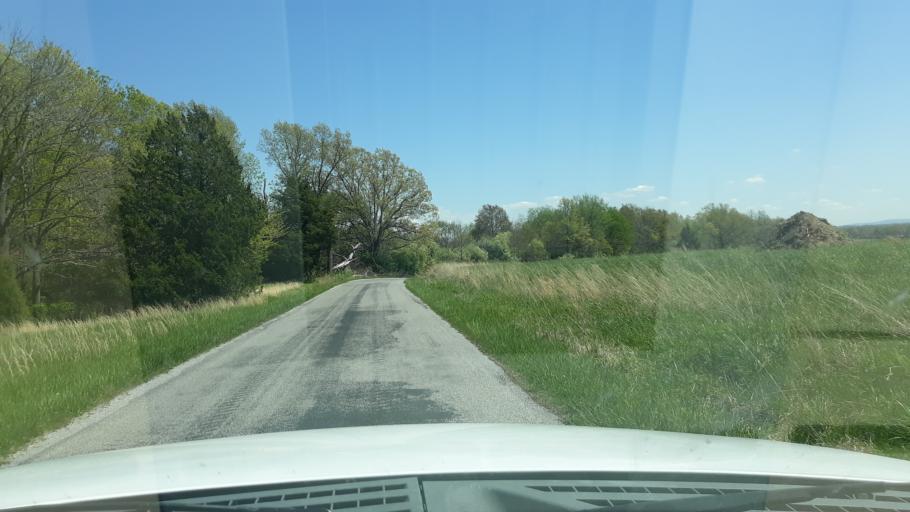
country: US
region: Illinois
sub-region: Saline County
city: Harrisburg
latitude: 37.8558
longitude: -88.6355
